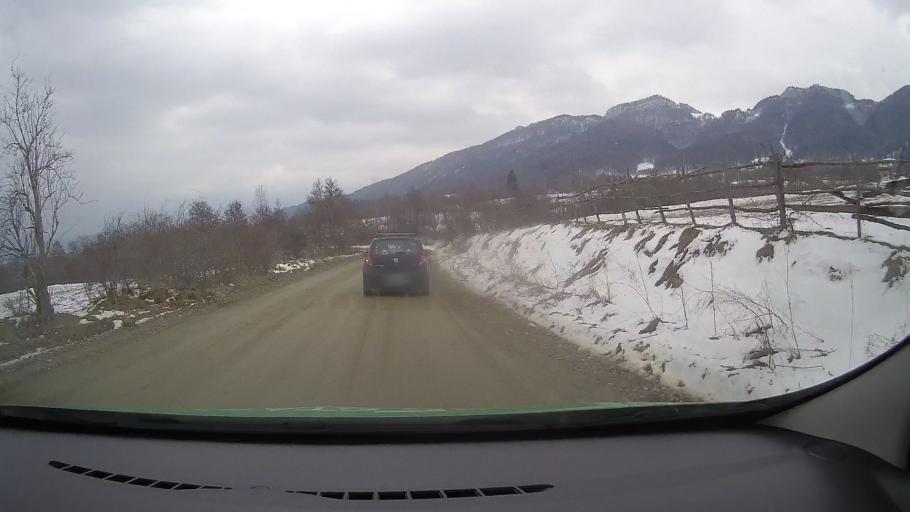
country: RO
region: Brasov
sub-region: Comuna Zarnesti
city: Zarnesti
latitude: 45.5434
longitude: 25.3246
